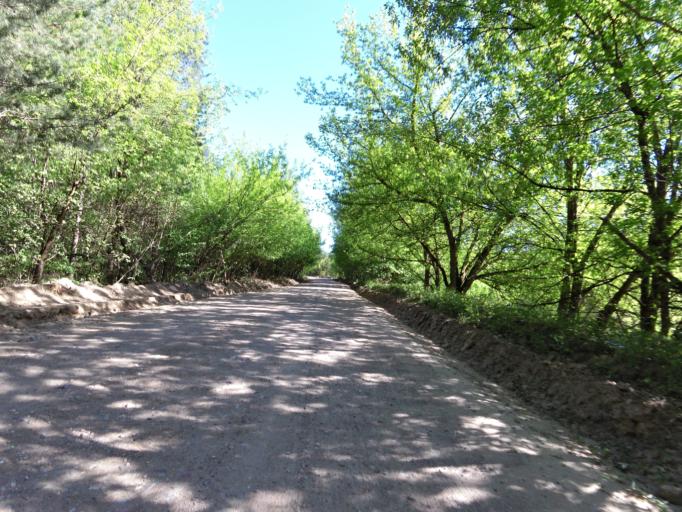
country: LT
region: Vilnius County
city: Pilaite
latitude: 54.6795
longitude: 25.1623
